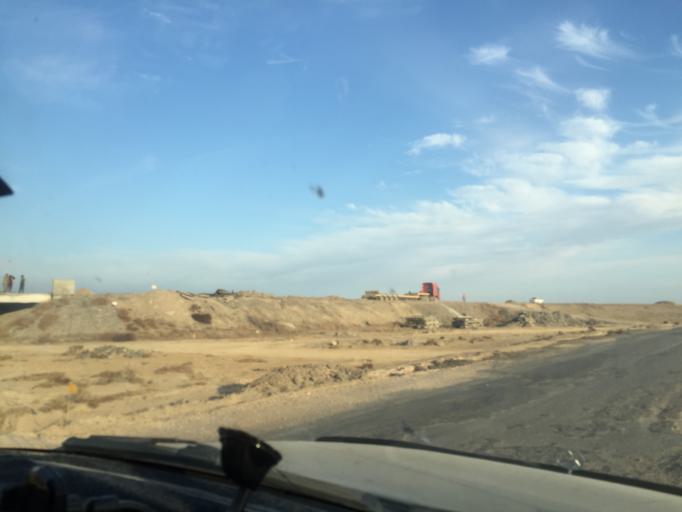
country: KZ
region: Almaty Oblysy
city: Ulken
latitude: 45.2435
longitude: 73.8218
